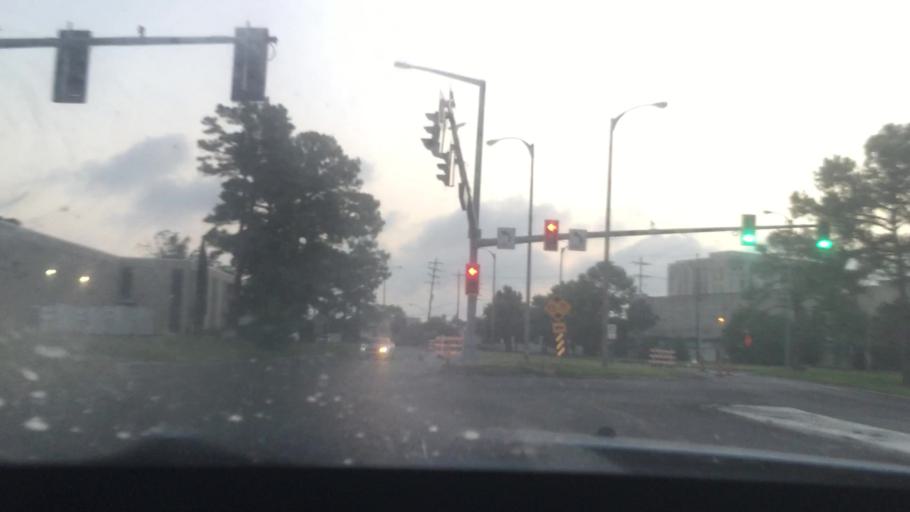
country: US
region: Louisiana
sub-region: West Baton Rouge Parish
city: Port Allen
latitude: 30.4619
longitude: -91.1893
